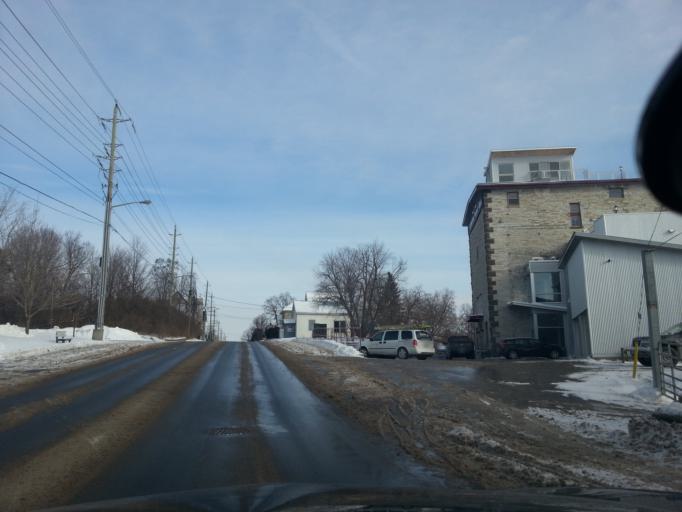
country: CA
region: Ontario
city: Carleton Place
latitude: 45.2269
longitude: -76.1971
